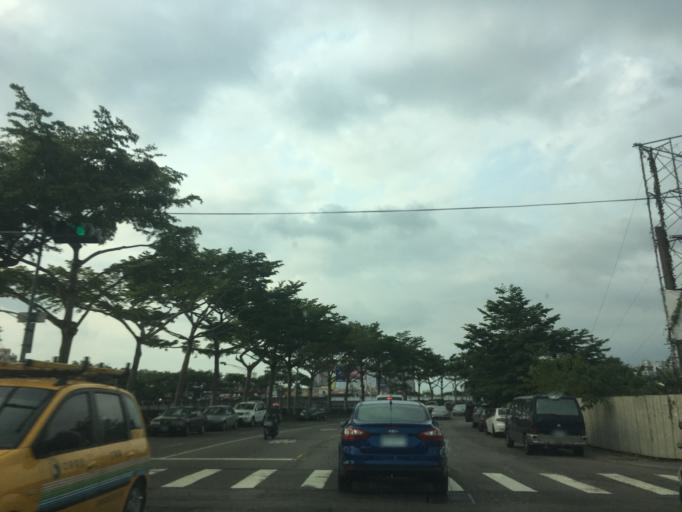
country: TW
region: Taiwan
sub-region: Taichung City
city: Taichung
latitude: 24.1624
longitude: 120.7046
